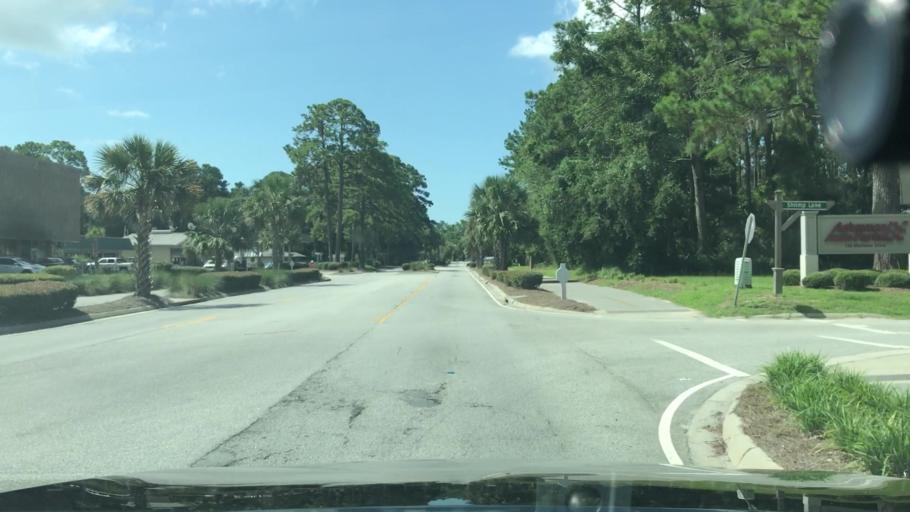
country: US
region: South Carolina
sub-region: Beaufort County
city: Hilton Head Island
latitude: 32.2095
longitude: -80.7027
